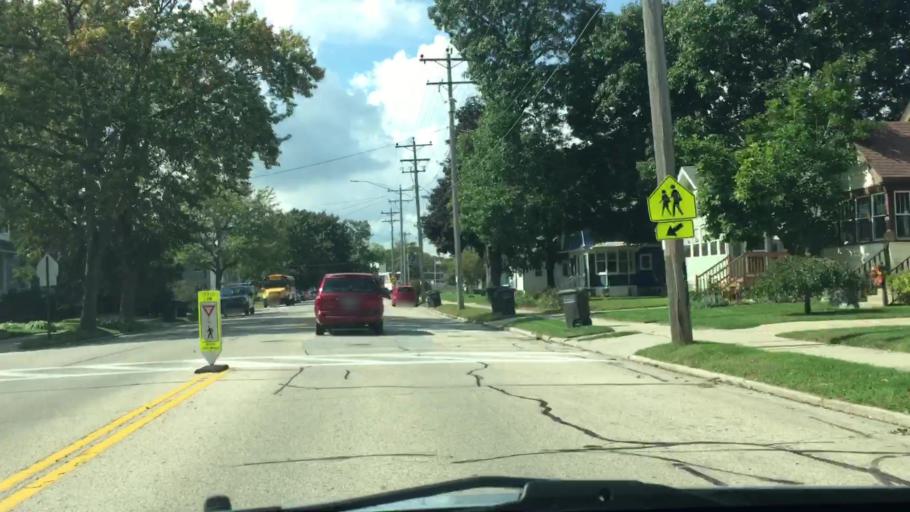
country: US
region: Wisconsin
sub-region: Waukesha County
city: Oconomowoc
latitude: 43.1094
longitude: -88.5053
